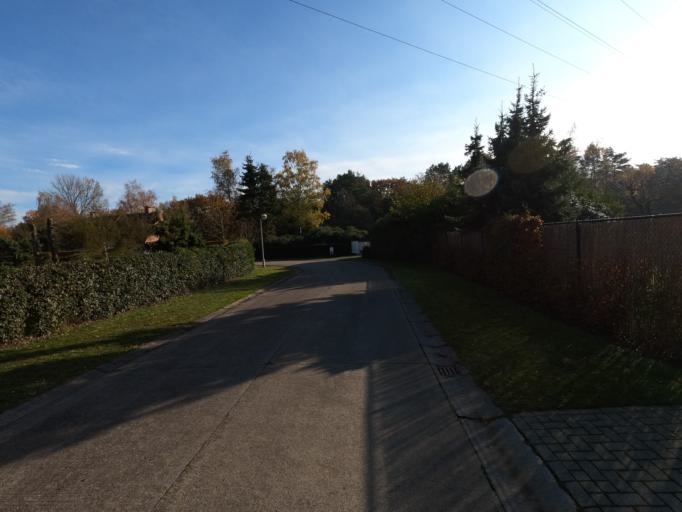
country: BE
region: Flanders
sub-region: Provincie Antwerpen
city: Brasschaat
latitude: 51.3393
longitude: 4.5391
